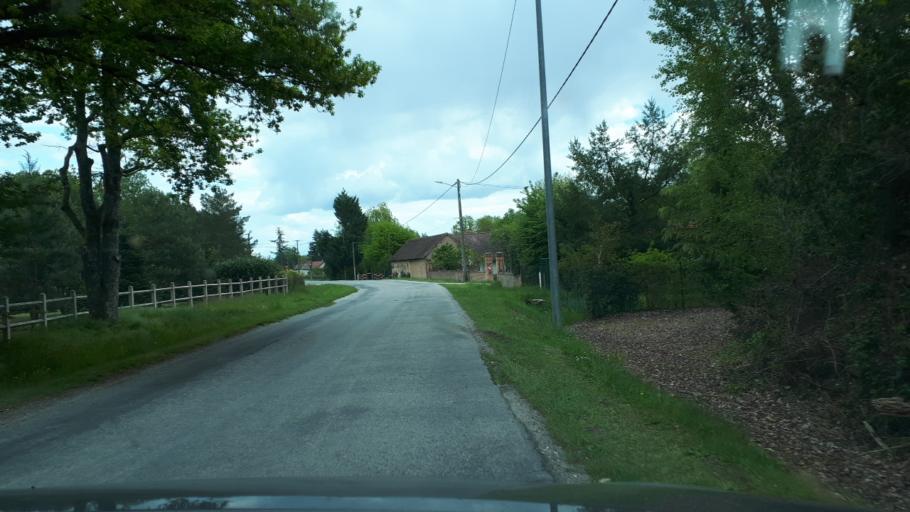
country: FR
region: Centre
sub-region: Departement du Loir-et-Cher
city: Souesmes
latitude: 47.5155
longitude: 2.1430
